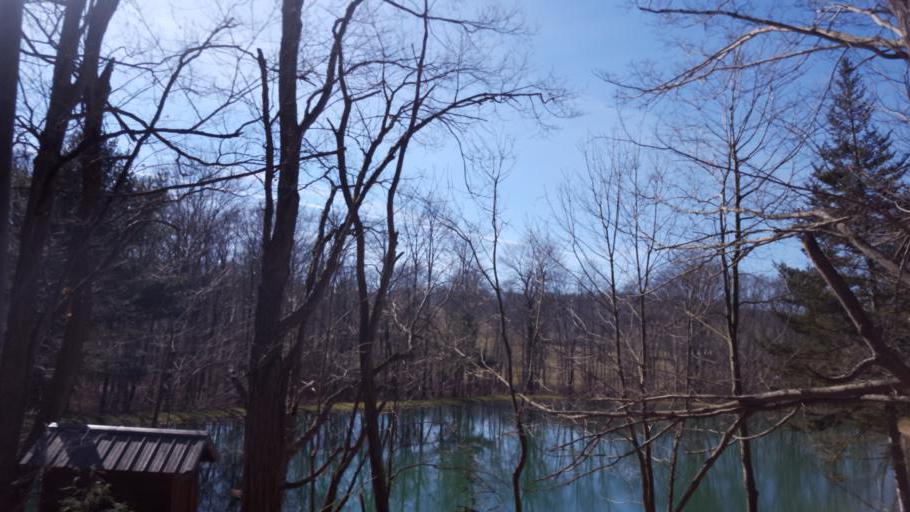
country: US
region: Ohio
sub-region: Knox County
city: Danville
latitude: 40.5340
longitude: -82.3129
